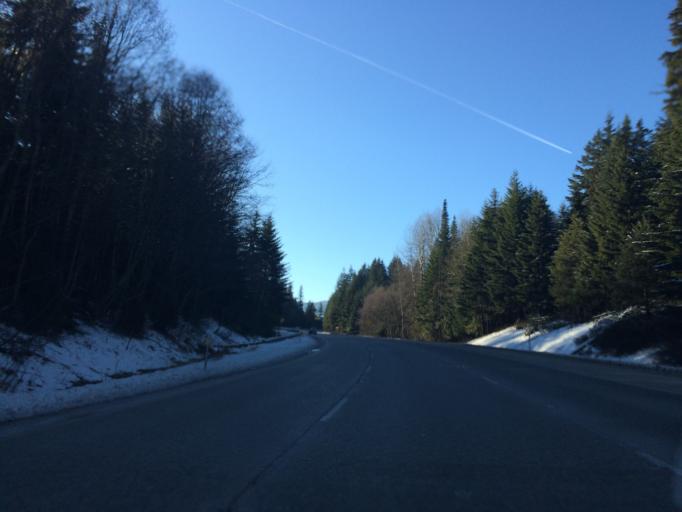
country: US
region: Washington
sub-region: Kittitas County
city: Cle Elum
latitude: 47.2700
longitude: -121.2349
